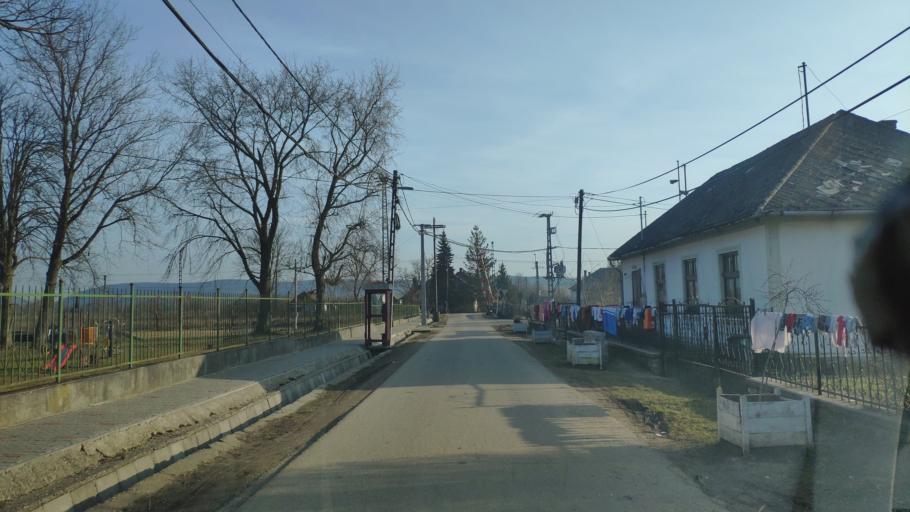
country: HU
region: Borsod-Abauj-Zemplen
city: Szendro
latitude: 48.5592
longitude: 20.7876
